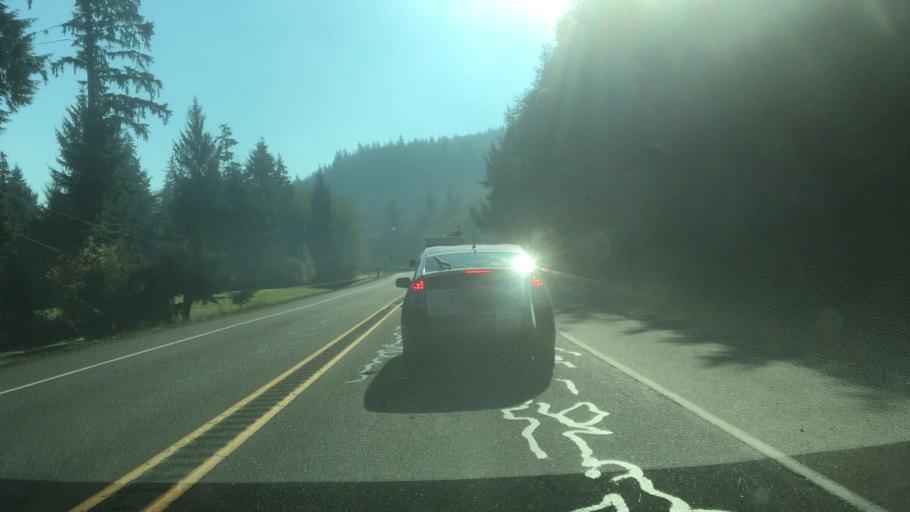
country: US
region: Washington
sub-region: Grays Harbor County
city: Central Park
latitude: 46.9200
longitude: -123.7183
